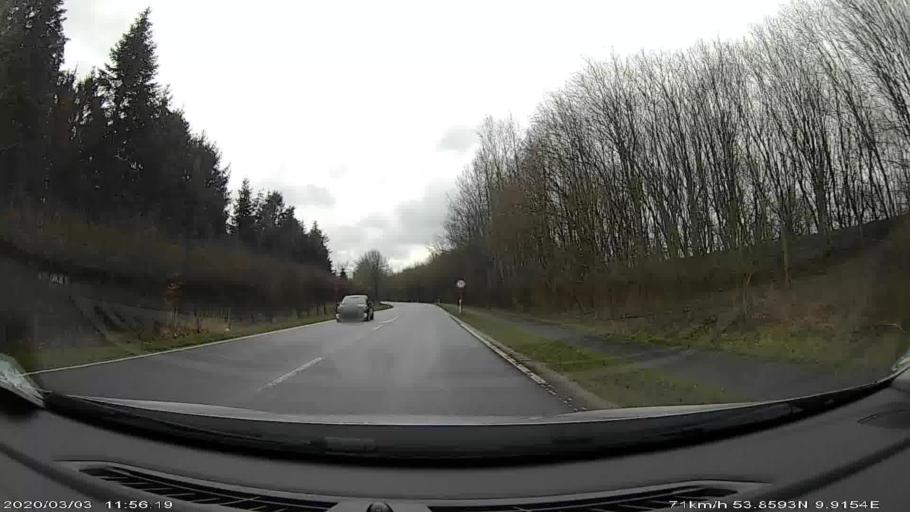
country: DE
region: Schleswig-Holstein
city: Nutzen
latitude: 53.8580
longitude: 9.9182
